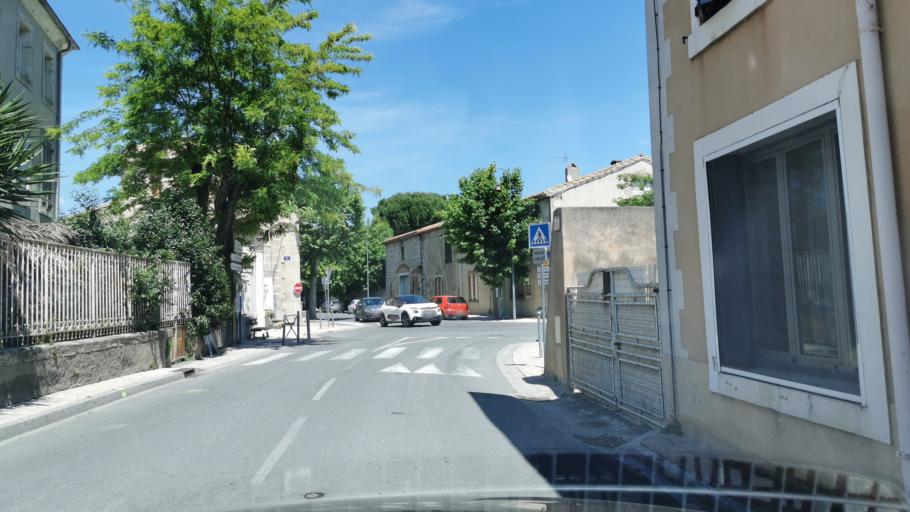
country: FR
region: Languedoc-Roussillon
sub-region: Departement de l'Aude
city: Moussan
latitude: 43.2441
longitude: 2.9974
